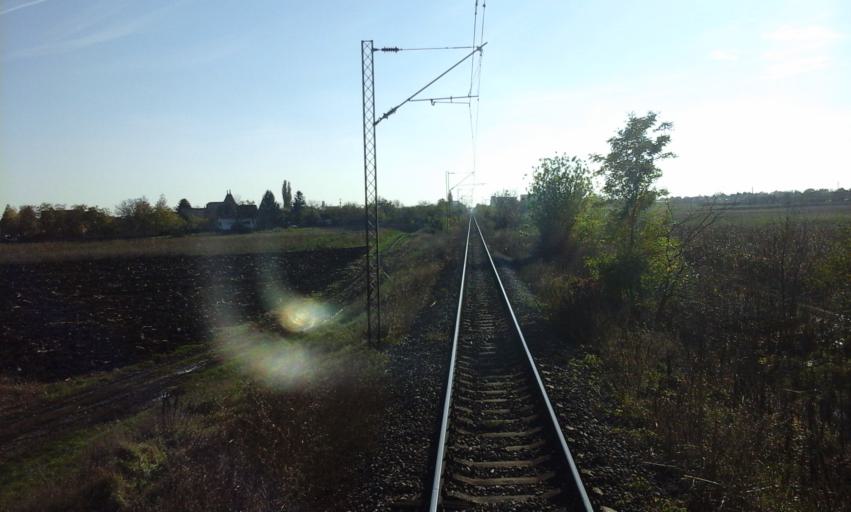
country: RS
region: Autonomna Pokrajina Vojvodina
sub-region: Severnobacki Okrug
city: Backa Topola
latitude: 45.8315
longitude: 19.6516
